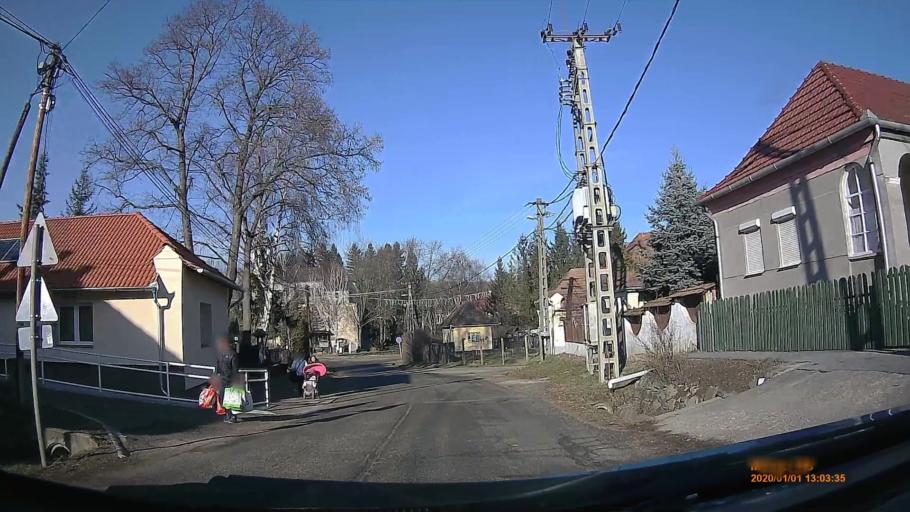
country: HU
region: Heves
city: Parad
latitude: 47.9421
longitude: 20.0235
